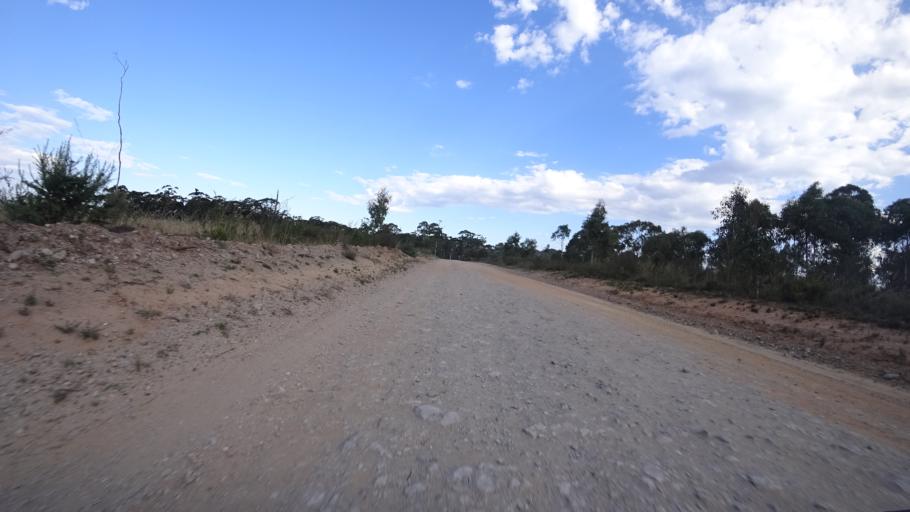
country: AU
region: New South Wales
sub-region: Lithgow
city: Lithgow
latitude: -33.4150
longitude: 150.2032
